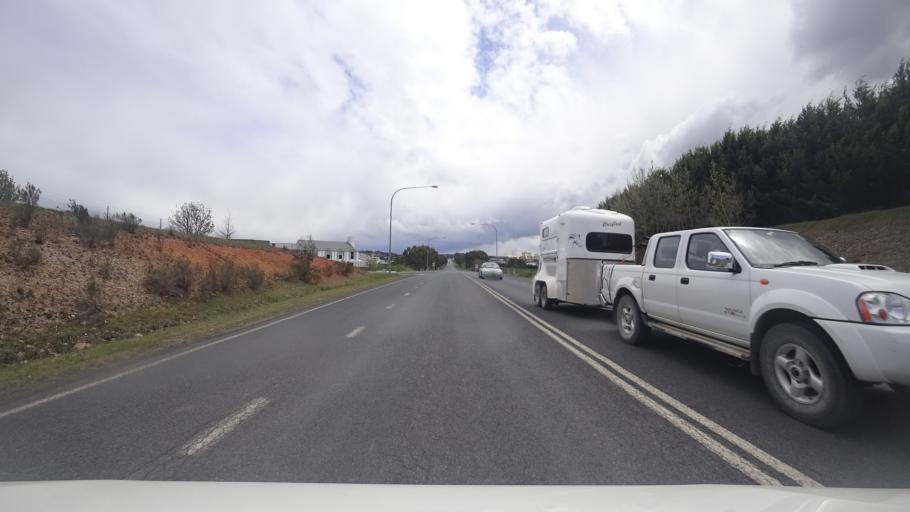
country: AU
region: New South Wales
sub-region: Oberon
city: Oberon
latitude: -33.7011
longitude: 149.8736
